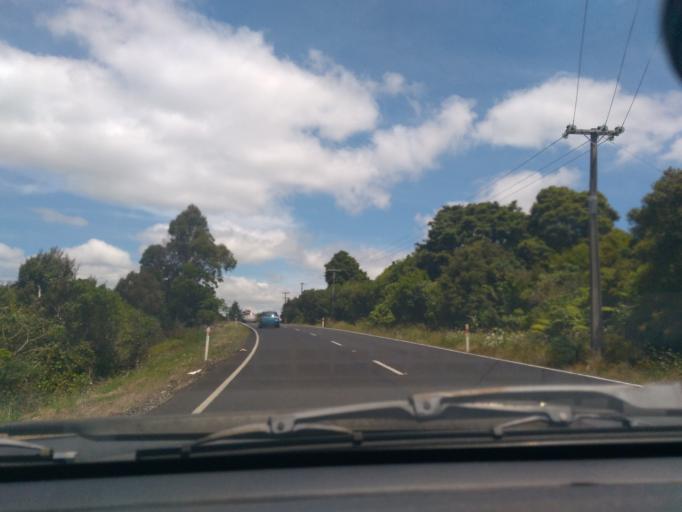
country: NZ
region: Northland
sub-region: Far North District
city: Kerikeri
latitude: -35.1460
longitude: 173.8821
